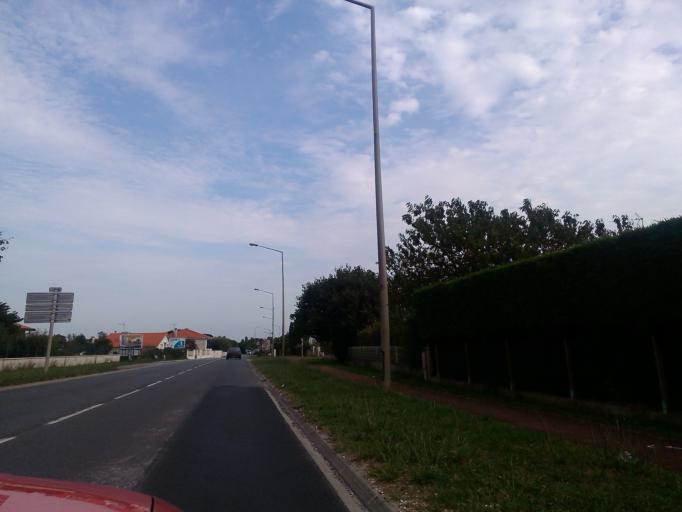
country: FR
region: Poitou-Charentes
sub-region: Departement de la Charente-Maritime
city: Saujon
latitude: 45.6750
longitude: -0.9454
